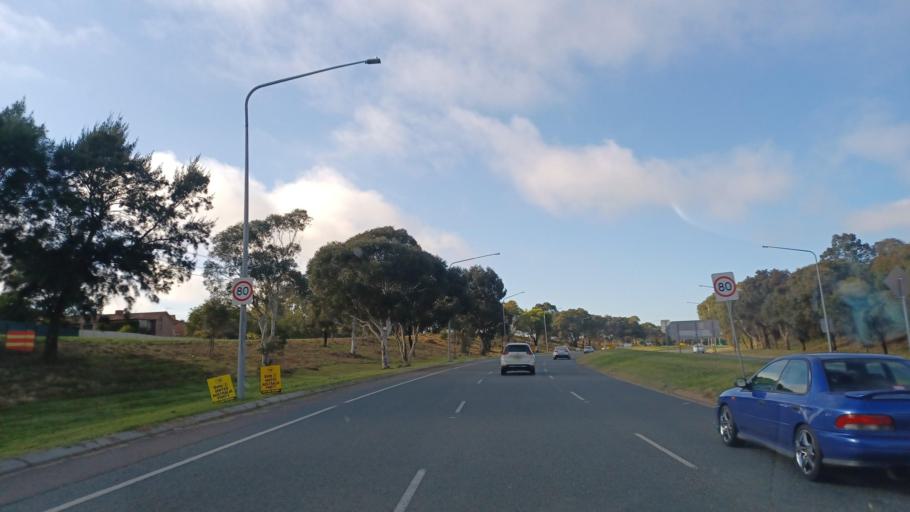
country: AU
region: Australian Capital Territory
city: Belconnen
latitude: -35.2229
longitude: 149.0714
